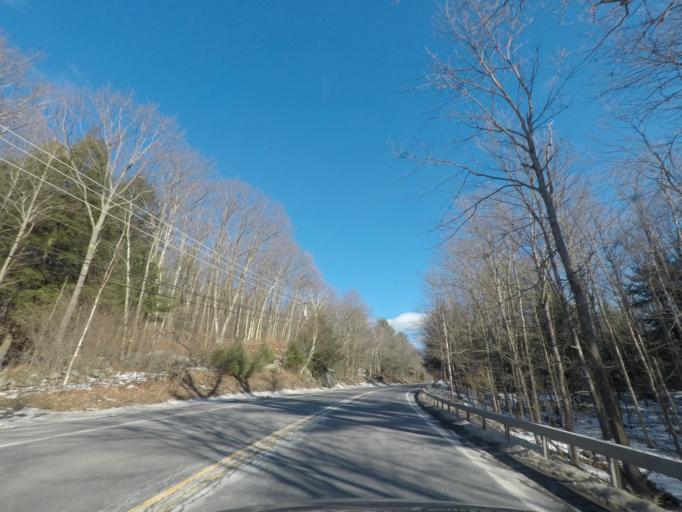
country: US
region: New York
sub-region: Columbia County
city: Chatham
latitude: 42.3198
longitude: -73.5115
